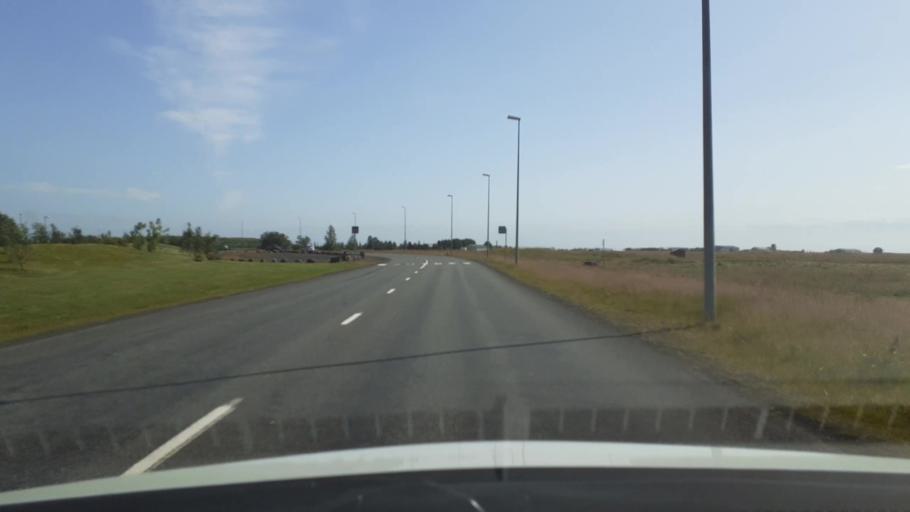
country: IS
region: South
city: Selfoss
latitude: 63.9231
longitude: -21.0080
